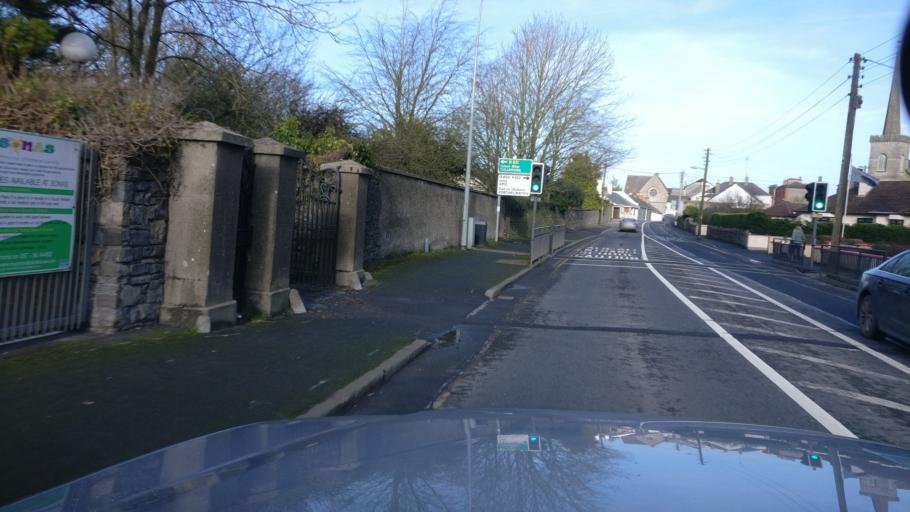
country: IE
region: Leinster
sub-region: Laois
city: Mountmellick
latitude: 53.1155
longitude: -7.3281
